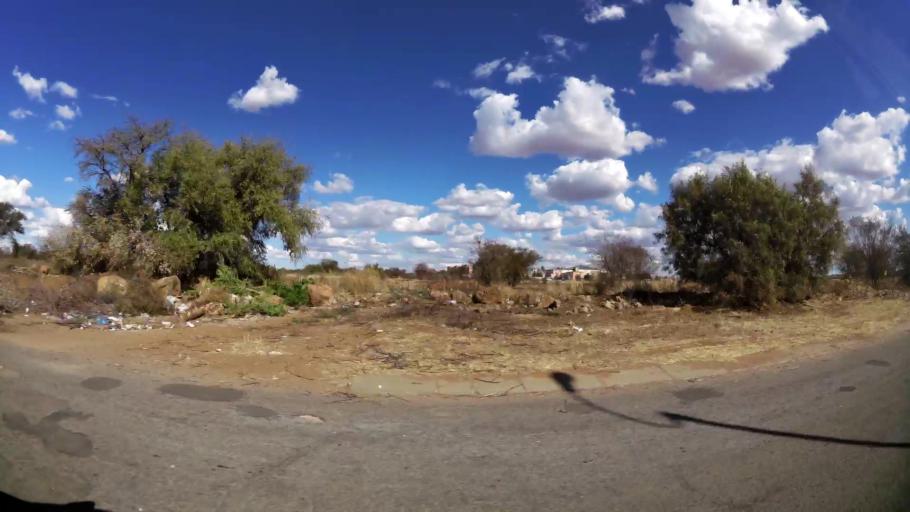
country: ZA
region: North-West
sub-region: Dr Kenneth Kaunda District Municipality
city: Klerksdorp
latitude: -26.8649
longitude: 26.6218
